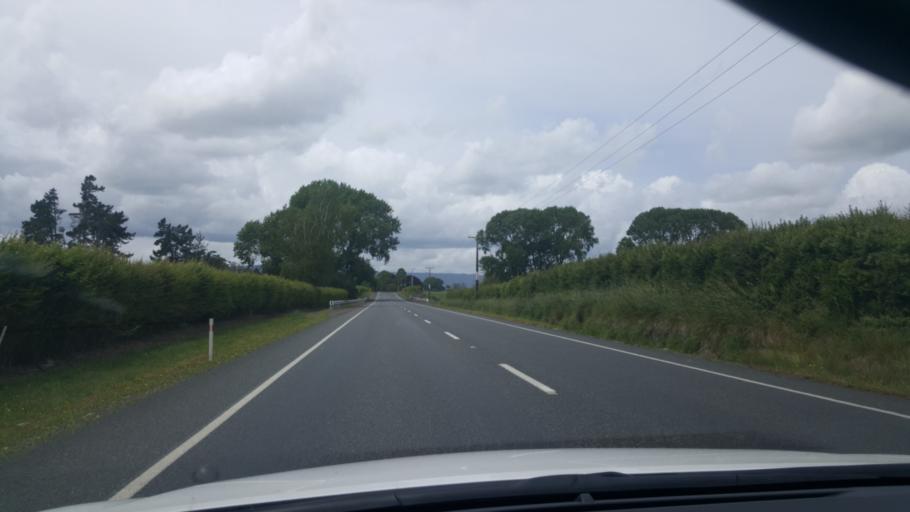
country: NZ
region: Waikato
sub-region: Matamata-Piako District
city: Matamata
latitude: -37.8804
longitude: 175.7475
